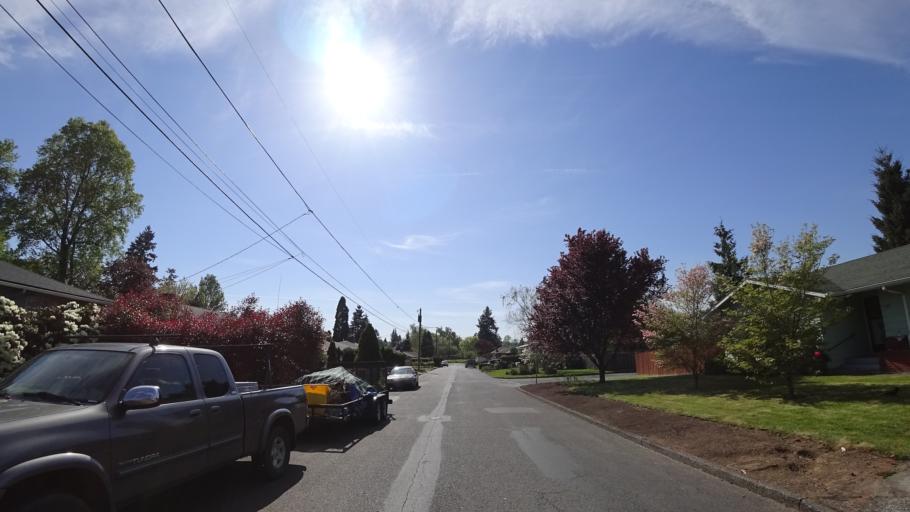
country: US
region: Oregon
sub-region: Clackamas County
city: Milwaukie
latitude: 45.4592
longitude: -122.6269
